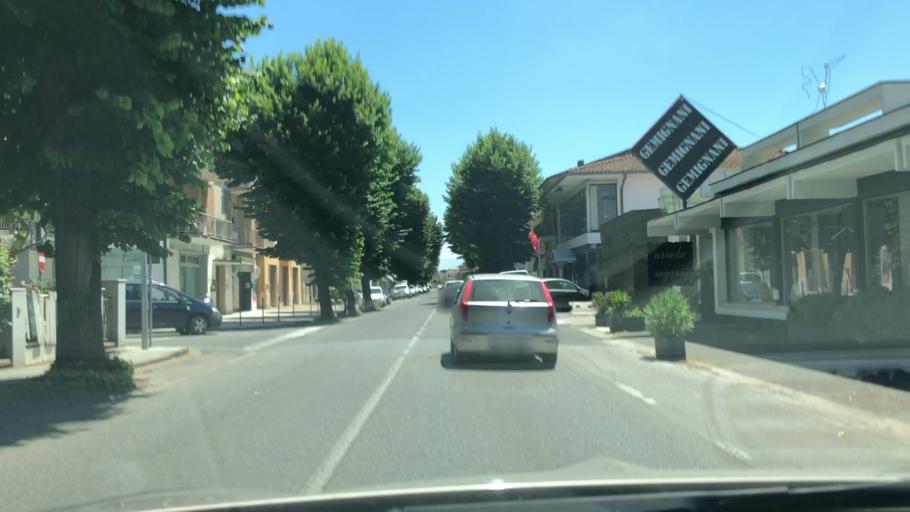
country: IT
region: Tuscany
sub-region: Province of Pisa
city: Ponsacco
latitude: 43.6263
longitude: 10.6295
